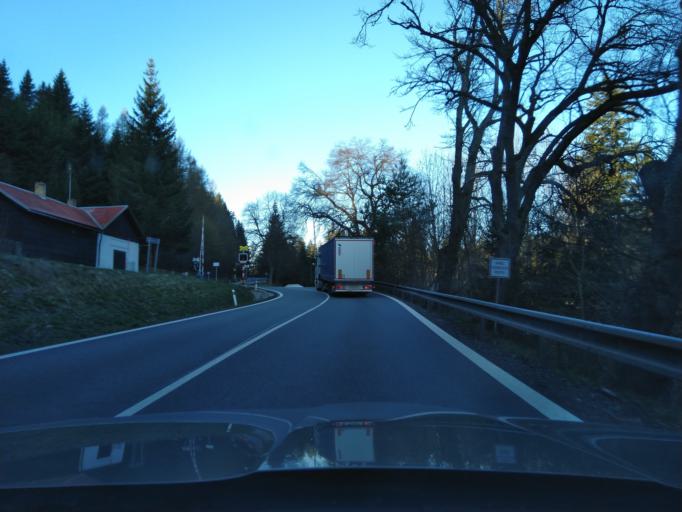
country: CZ
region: Jihocesky
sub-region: Okres Prachatice
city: Vimperk
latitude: 49.0490
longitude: 13.7642
